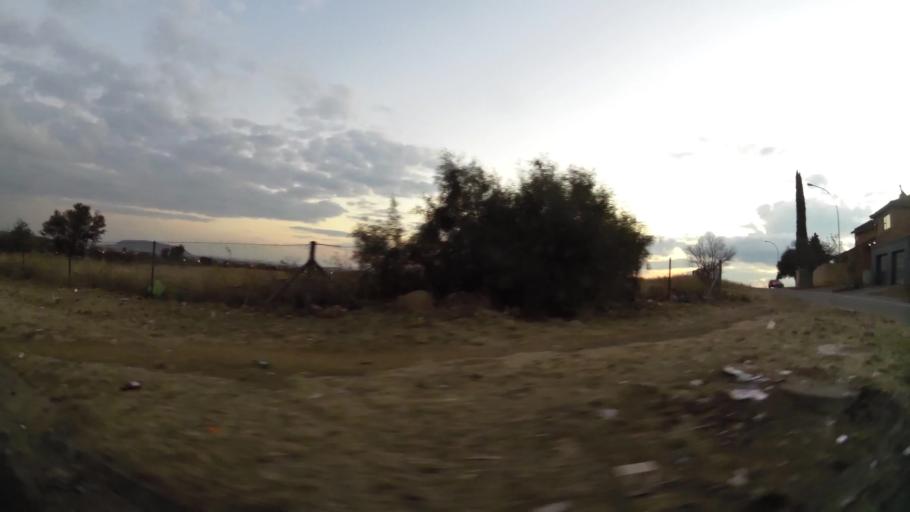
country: ZA
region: Orange Free State
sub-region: Mangaung Metropolitan Municipality
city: Bloemfontein
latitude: -29.1608
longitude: 26.1953
